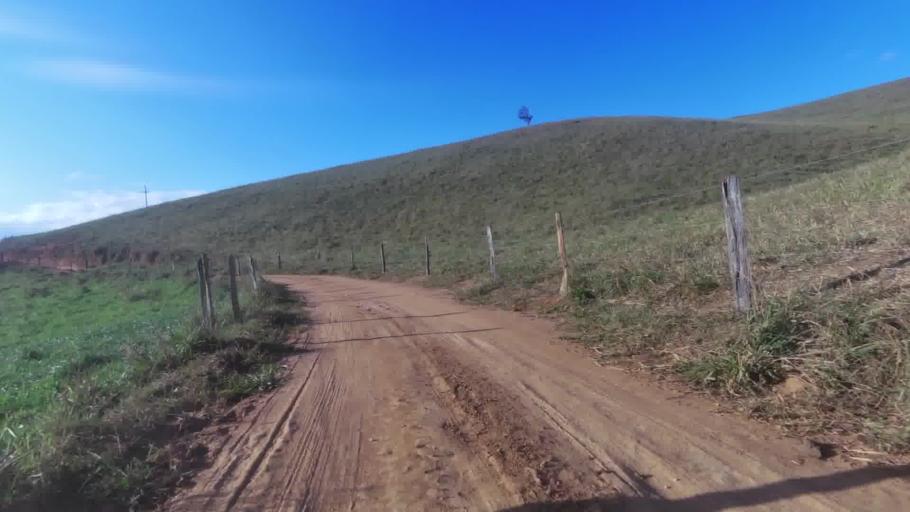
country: BR
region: Espirito Santo
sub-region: Marataizes
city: Marataizes
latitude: -21.1576
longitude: -41.0351
